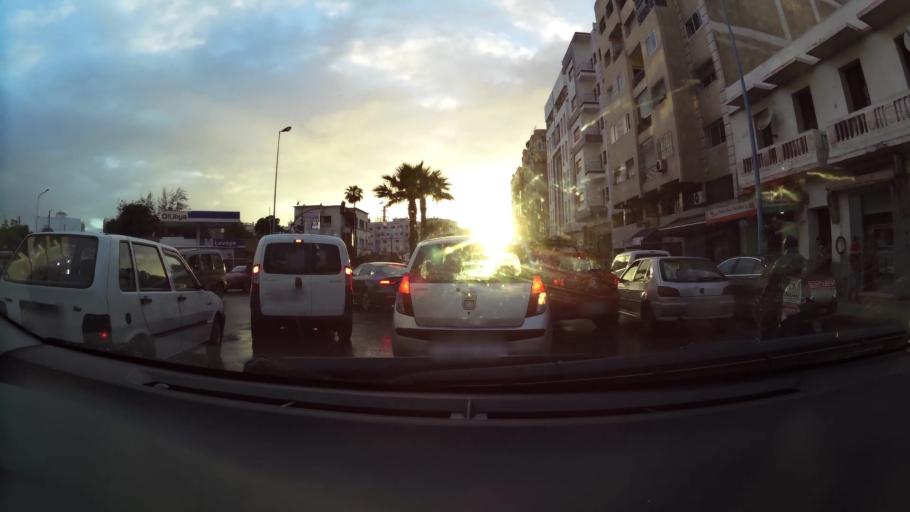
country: MA
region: Grand Casablanca
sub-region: Casablanca
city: Casablanca
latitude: 33.5871
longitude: -7.5945
